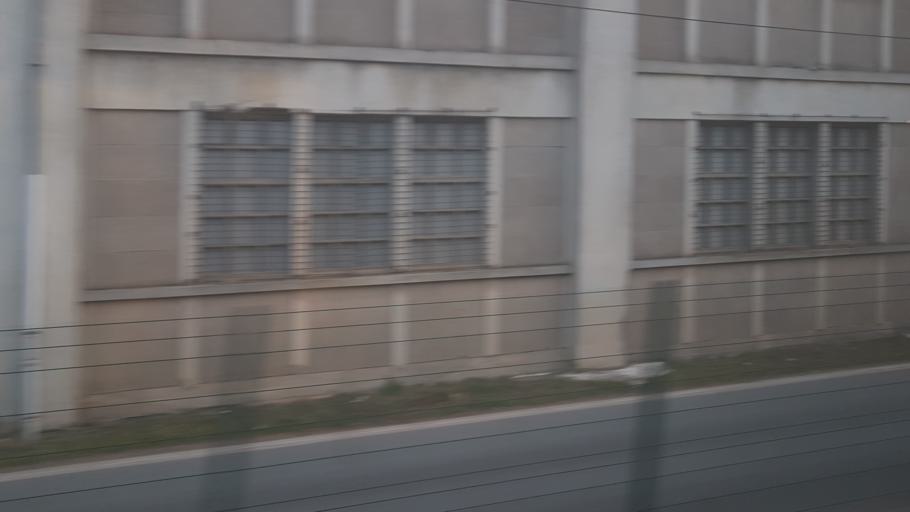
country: FR
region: Lorraine
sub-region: Departement des Vosges
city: Nomexy
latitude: 48.3050
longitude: 6.3896
